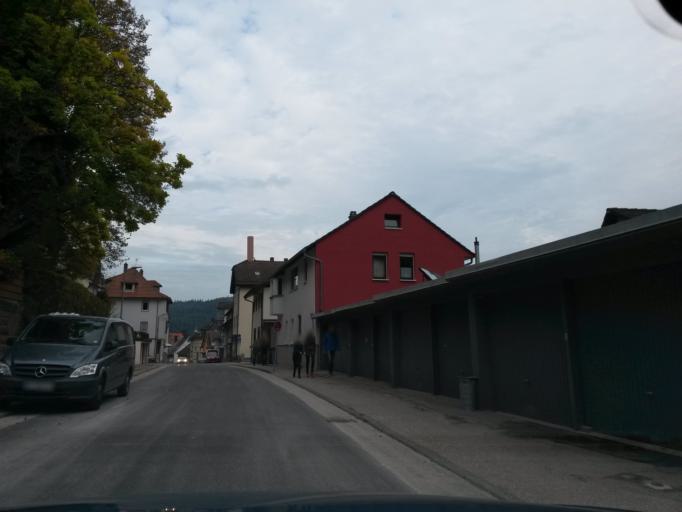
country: DE
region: Baden-Wuerttemberg
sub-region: Karlsruhe Region
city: Bad Herrenalb
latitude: 48.7951
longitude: 8.4333
